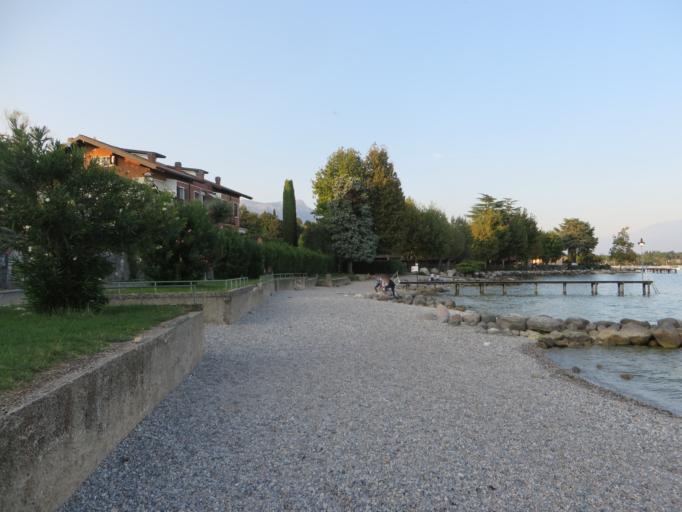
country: IT
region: Lombardy
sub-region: Provincia di Brescia
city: San Felice del Benaco
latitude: 45.5766
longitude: 10.5533
